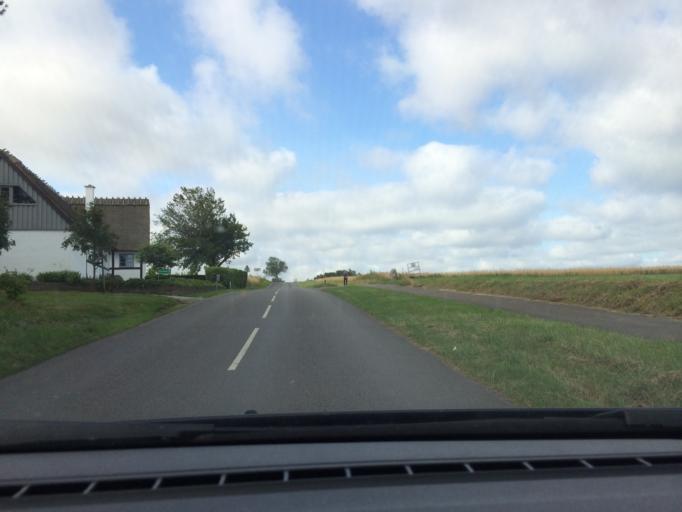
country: DK
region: Zealand
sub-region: Vordingborg Kommune
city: Stege
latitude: 55.0289
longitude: 12.2929
